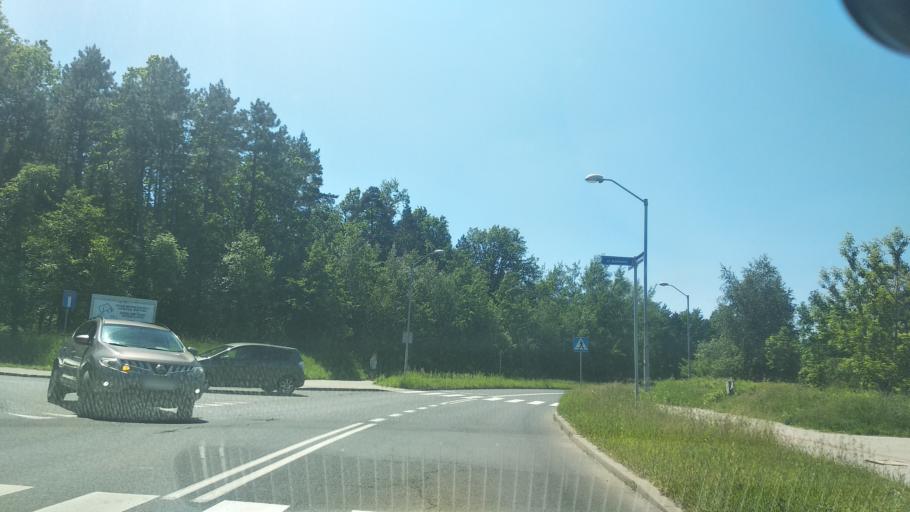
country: PL
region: Silesian Voivodeship
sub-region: Swietochlowice
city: Swietochlowice
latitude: 50.2498
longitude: 18.9194
